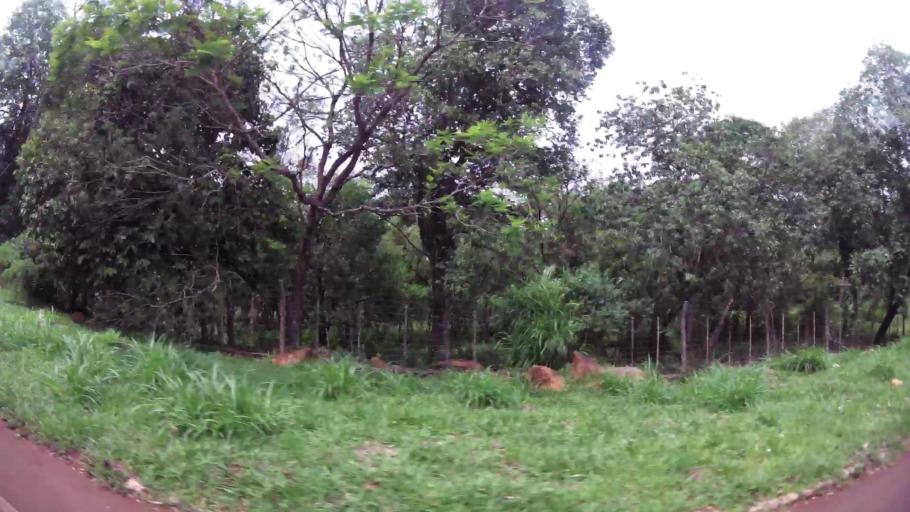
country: PY
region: Alto Parana
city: Presidente Franco
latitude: -25.5593
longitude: -54.6317
